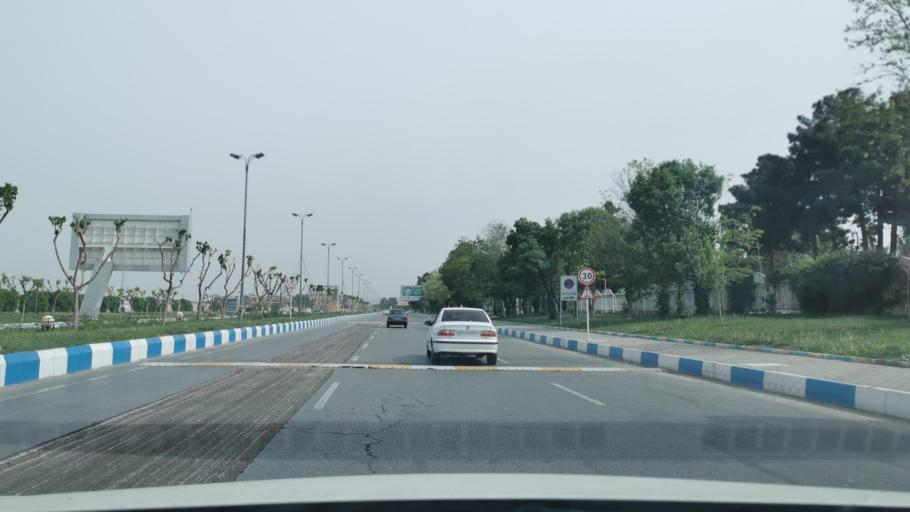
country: IR
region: Razavi Khorasan
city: Mashhad
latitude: 36.2386
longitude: 59.6280
